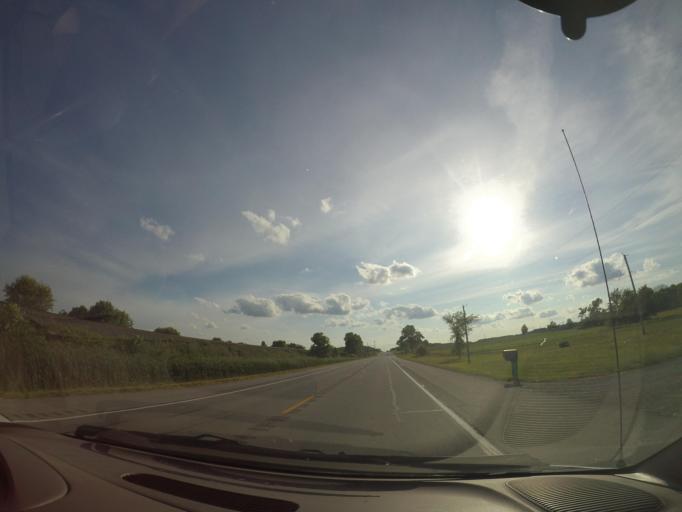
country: US
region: Indiana
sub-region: DeKalb County
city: Butler
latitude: 41.4379
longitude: -84.8095
